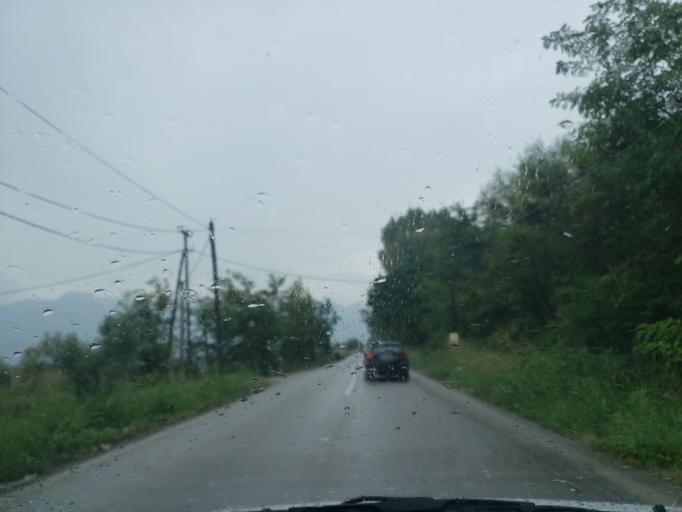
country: GR
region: Central Greece
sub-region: Nomos Fthiotidos
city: Anthili
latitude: 38.8444
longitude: 22.4408
